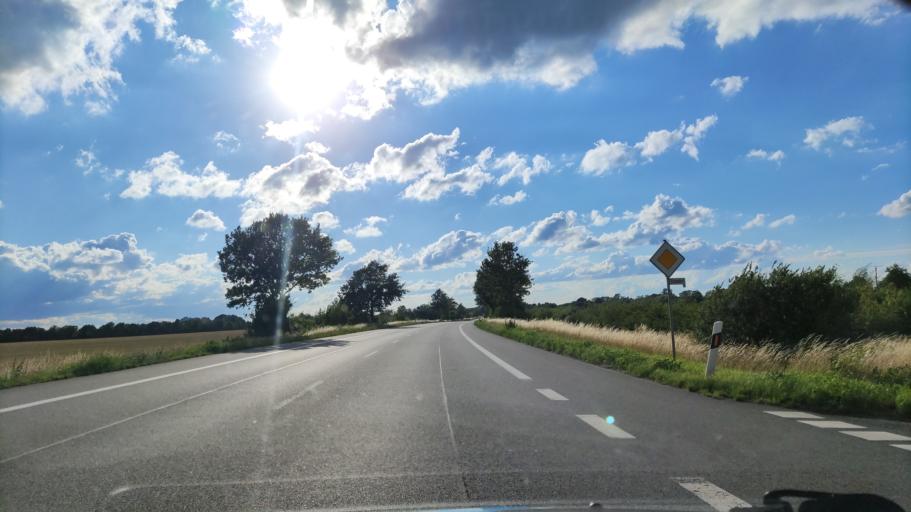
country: DE
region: North Rhine-Westphalia
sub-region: Regierungsbezirk Munster
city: Drensteinfurt
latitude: 51.7904
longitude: 7.7721
